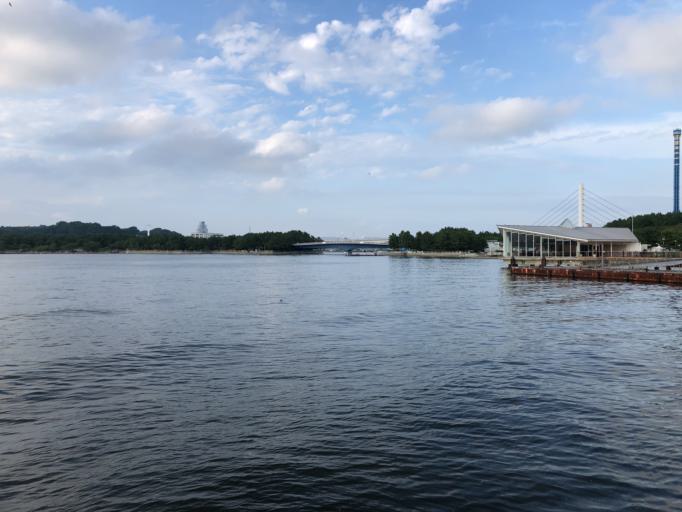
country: JP
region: Kanagawa
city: Yokosuka
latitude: 35.3357
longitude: 139.6408
